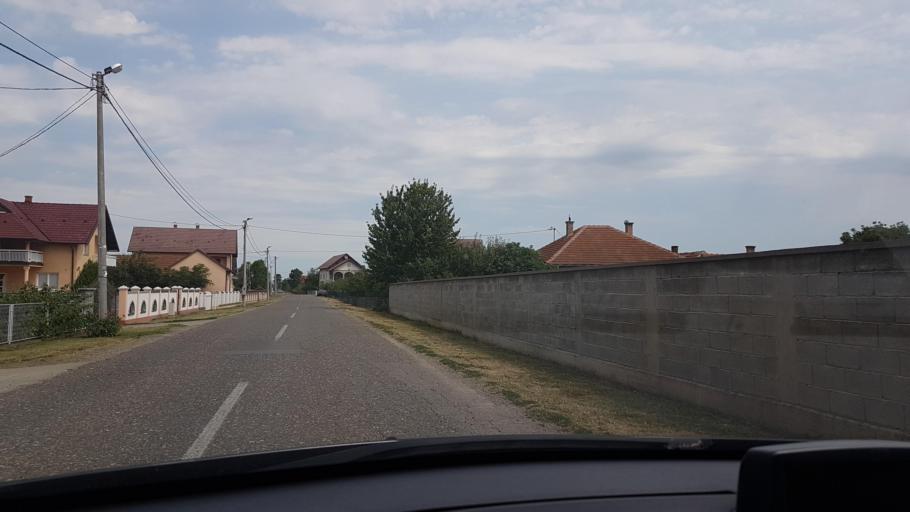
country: BA
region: Republika Srpska
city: Dvorovi
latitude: 44.8131
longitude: 19.2175
